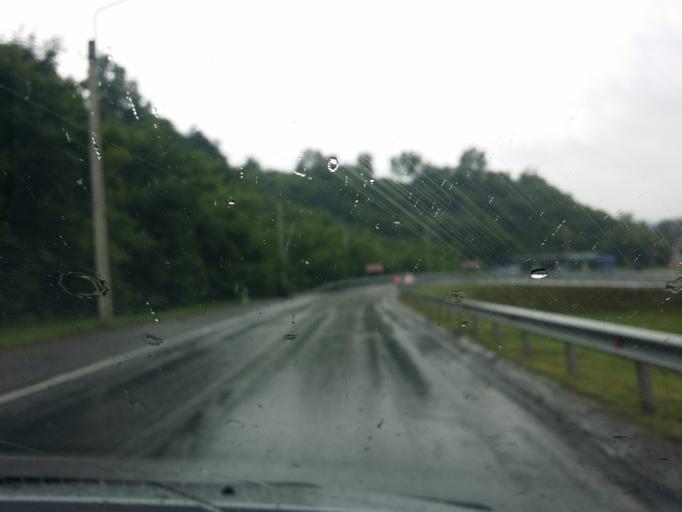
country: RU
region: Altai Krai
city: Zaton
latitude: 53.3221
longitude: 83.7868
